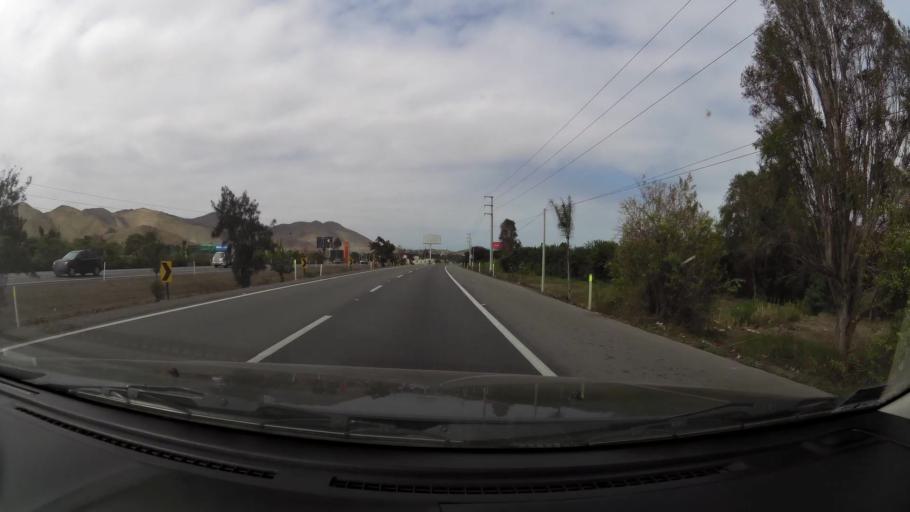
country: PE
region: Lima
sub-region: Provincia de Canete
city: Mala
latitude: -12.7231
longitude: -76.6185
